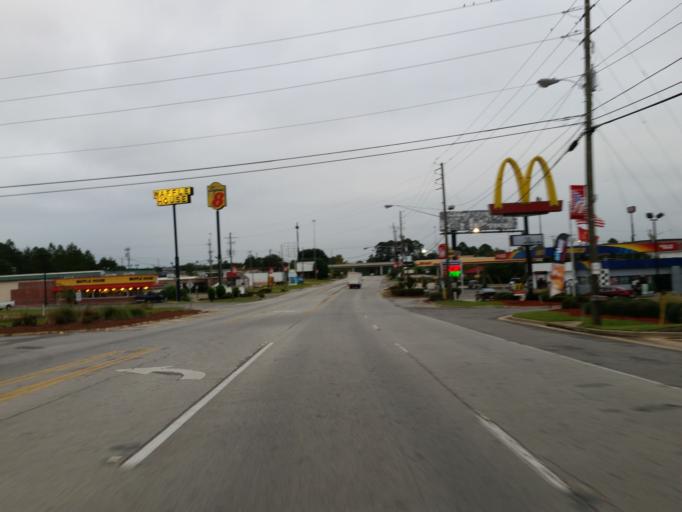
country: US
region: Georgia
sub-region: Turner County
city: Ashburn
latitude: 31.7102
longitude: -83.6417
